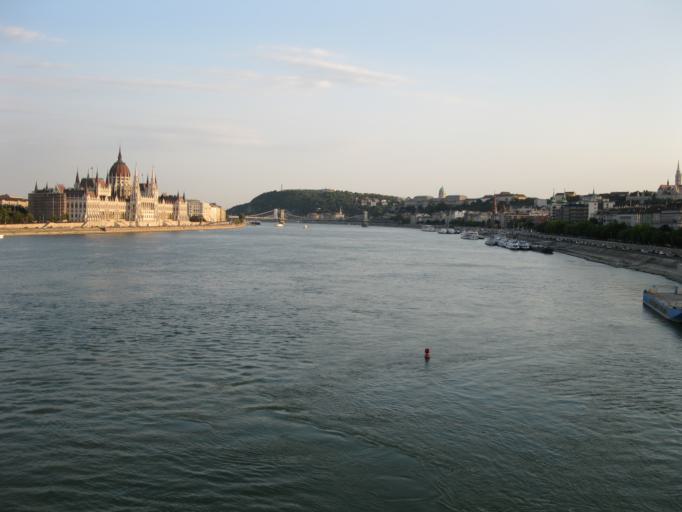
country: HU
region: Budapest
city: Budapest II. keruelet
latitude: 47.5146
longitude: 19.0412
